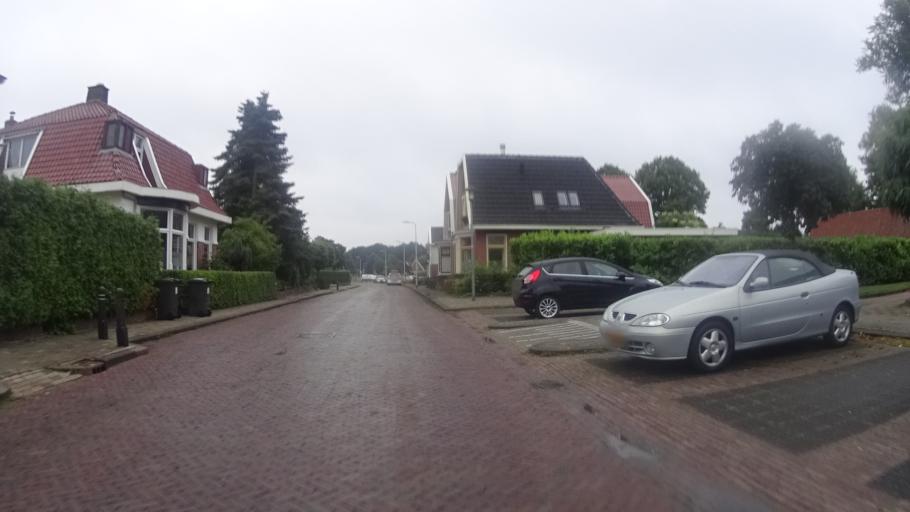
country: NL
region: Groningen
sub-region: Gemeente  Oldambt
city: Winschoten
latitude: 53.1759
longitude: 6.9728
